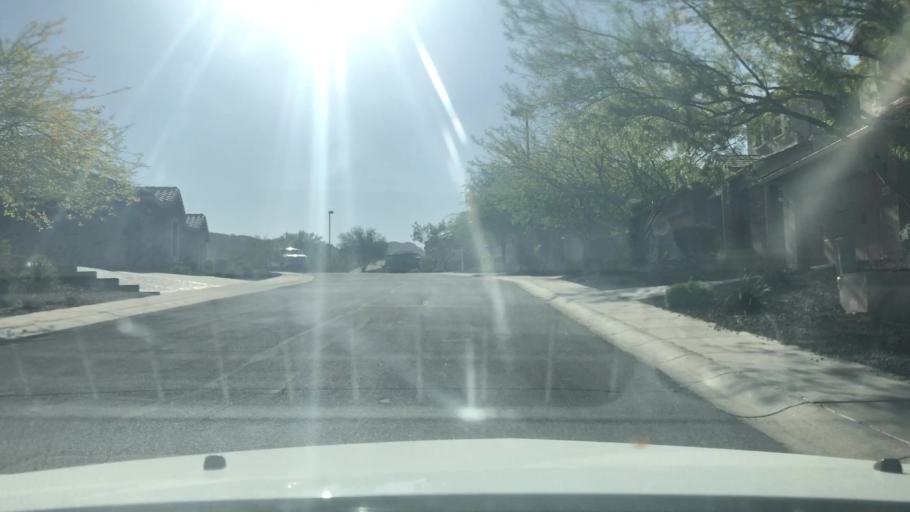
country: US
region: Arizona
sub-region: Maricopa County
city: Anthem
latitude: 33.7356
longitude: -112.0959
